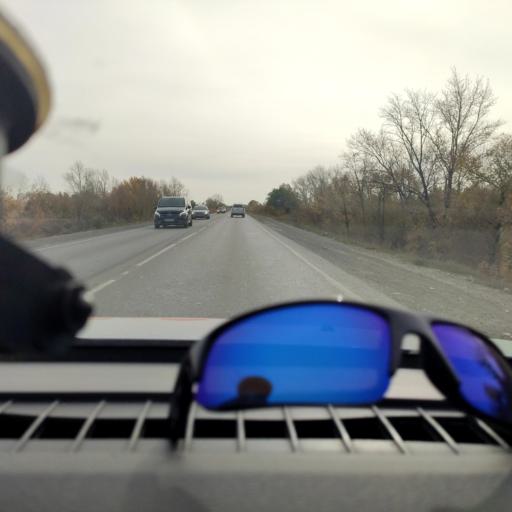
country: RU
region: Samara
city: Samara
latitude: 53.1054
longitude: 50.1361
